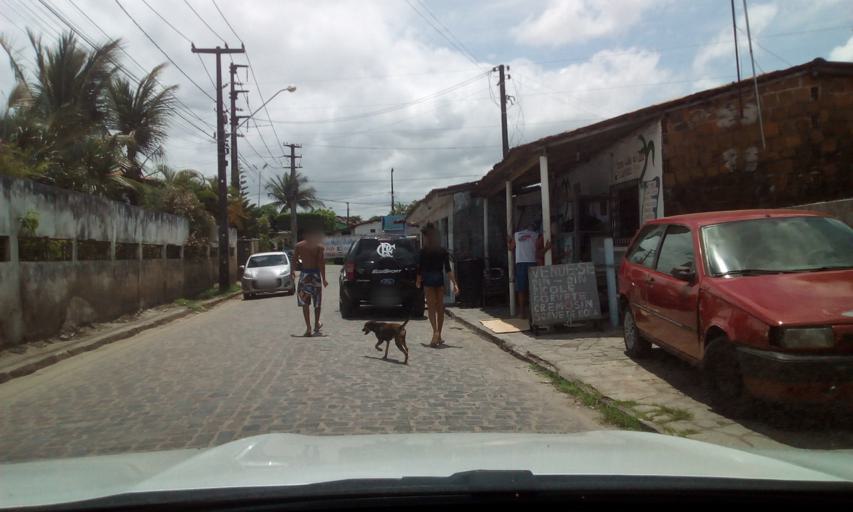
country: BR
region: Paraiba
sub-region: Bayeux
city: Bayeux
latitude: -7.1781
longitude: -34.8915
